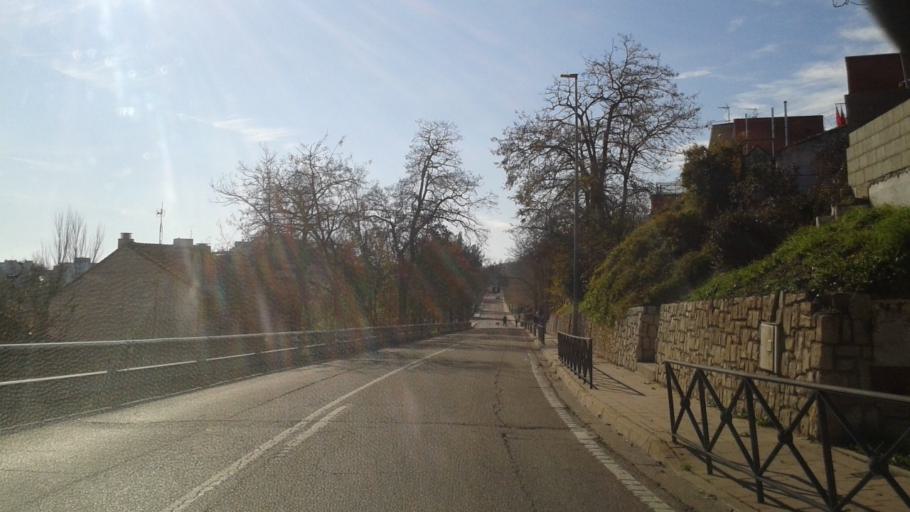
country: ES
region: Castille and Leon
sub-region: Provincia de Valladolid
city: Valladolid
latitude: 41.6693
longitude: -4.7364
